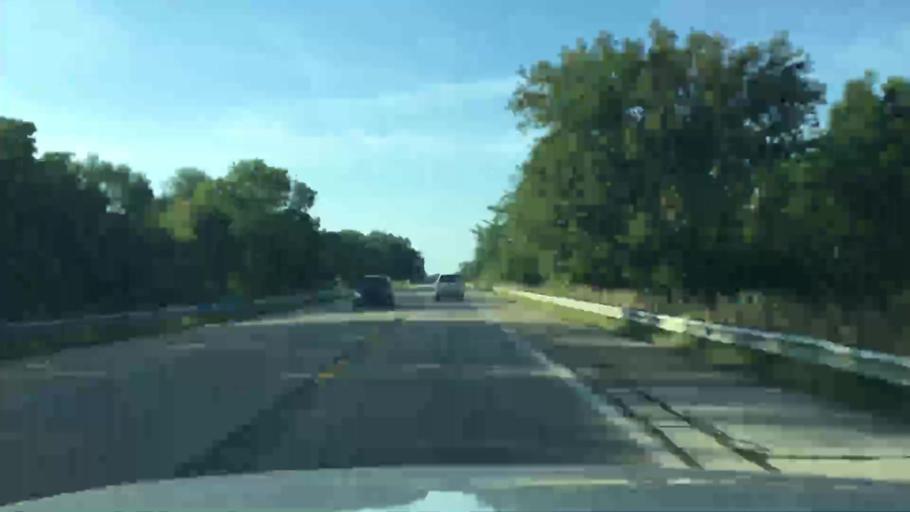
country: US
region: Michigan
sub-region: Jackson County
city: Vandercook Lake
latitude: 42.1072
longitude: -84.3640
